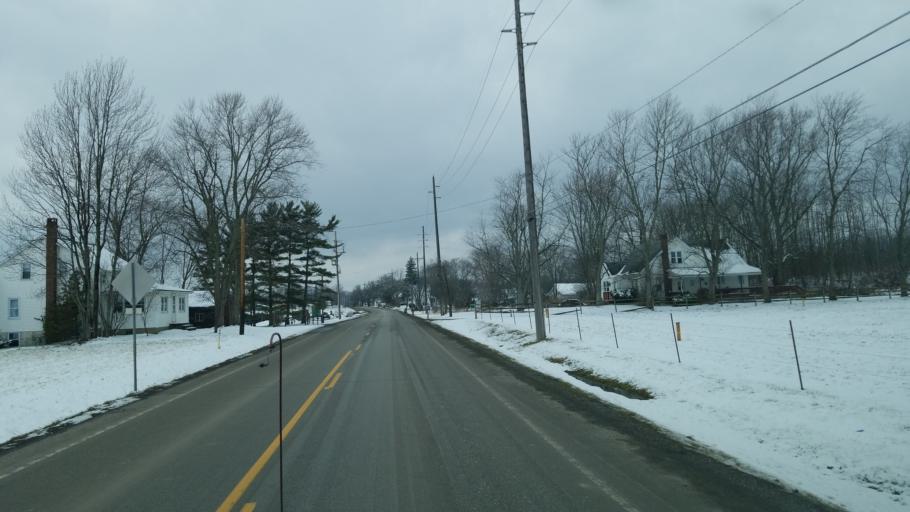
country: US
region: Ohio
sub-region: Geauga County
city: Middlefield
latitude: 41.4494
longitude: -81.0737
